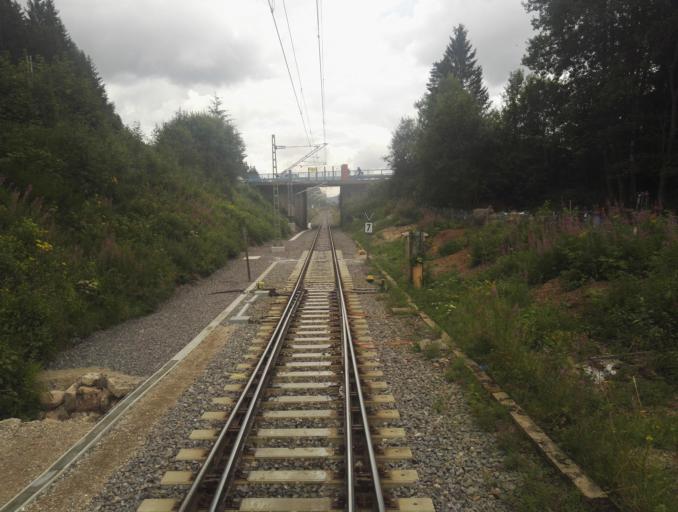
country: DE
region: Baden-Wuerttemberg
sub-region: Freiburg Region
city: Schluchsee
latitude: 47.8314
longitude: 8.1379
